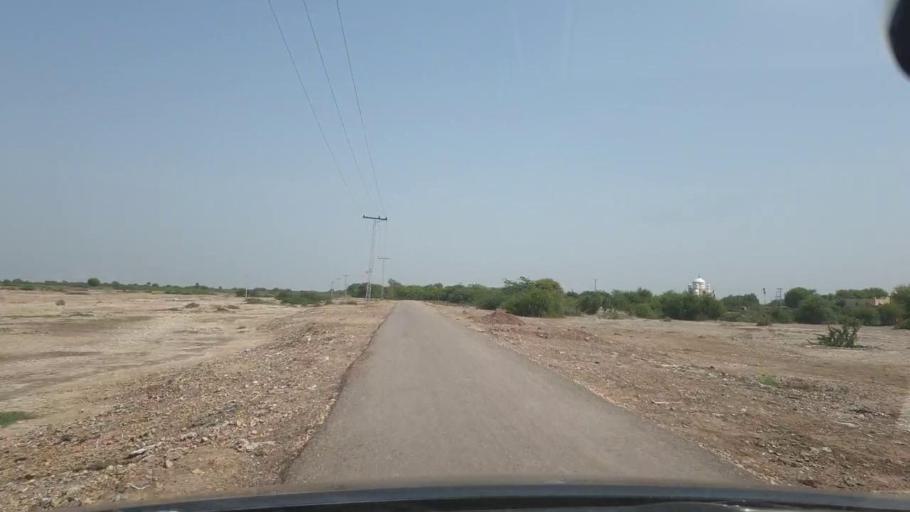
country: PK
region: Sindh
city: Naukot
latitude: 24.8137
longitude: 69.2192
